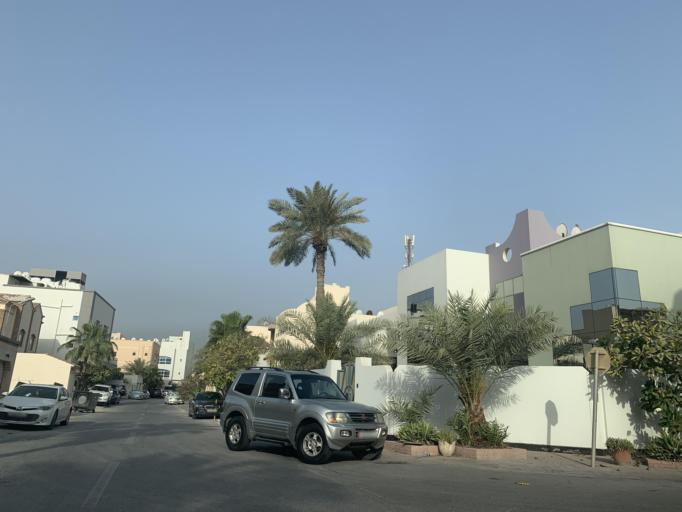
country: BH
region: Northern
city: Madinat `Isa
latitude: 26.1945
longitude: 50.5635
